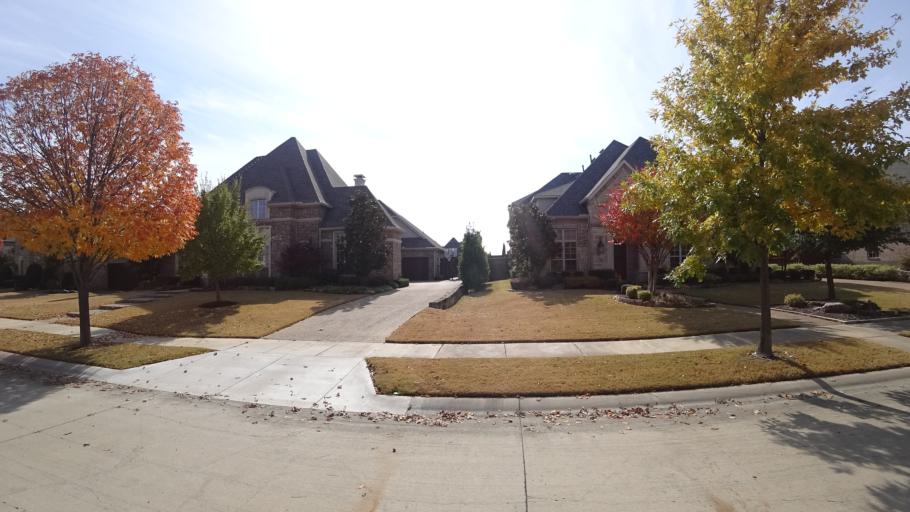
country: US
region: Texas
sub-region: Denton County
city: The Colony
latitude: 33.0417
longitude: -96.8888
